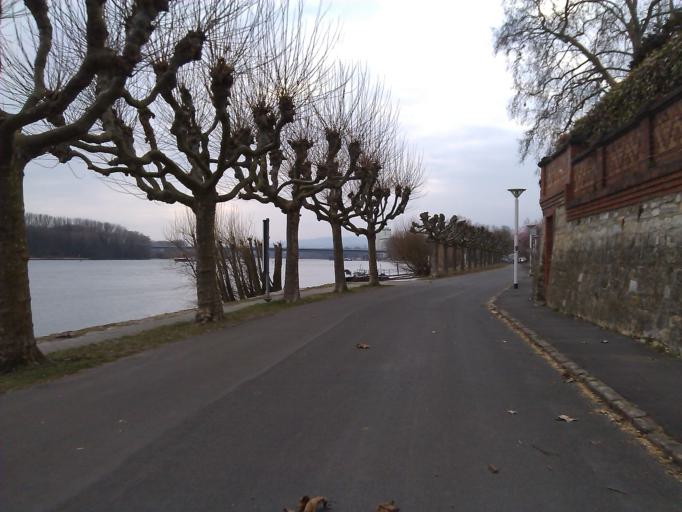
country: DE
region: Hesse
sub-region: Regierungsbezirk Darmstadt
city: Wiesbaden
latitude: 50.0378
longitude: 8.2288
